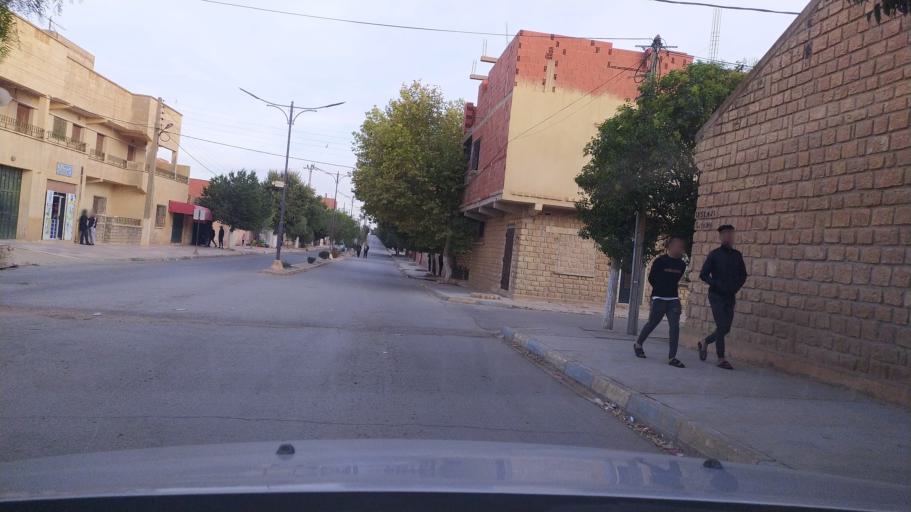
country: DZ
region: Tiaret
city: Frenda
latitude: 34.8984
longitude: 1.2379
